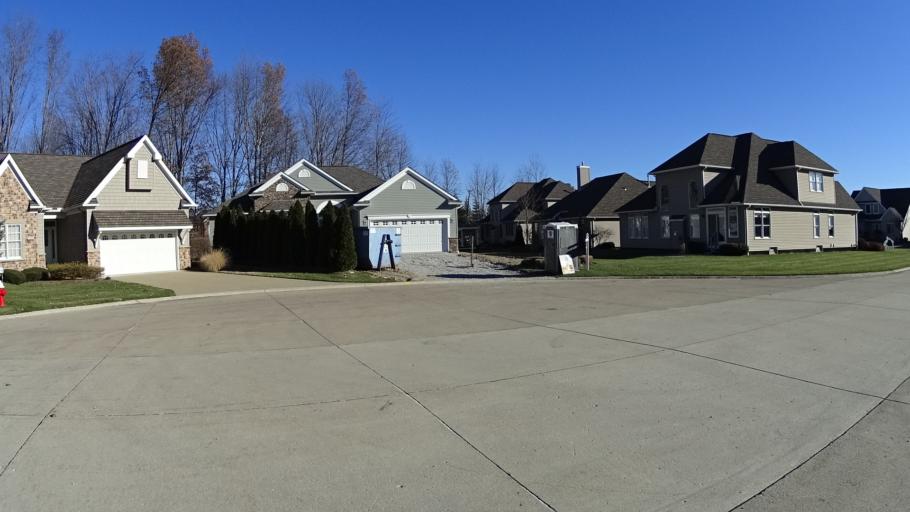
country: US
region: Ohio
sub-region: Lorain County
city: Avon Center
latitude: 41.4408
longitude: -81.9907
